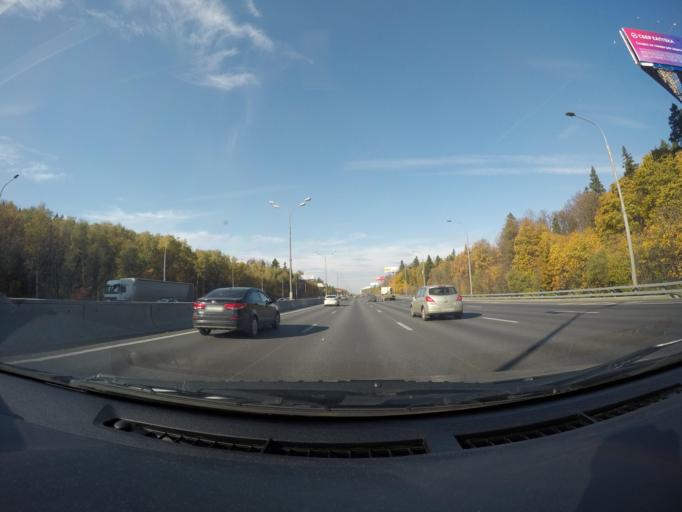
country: RU
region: Moscow
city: Gol'yanovo
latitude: 55.8486
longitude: 37.7920
